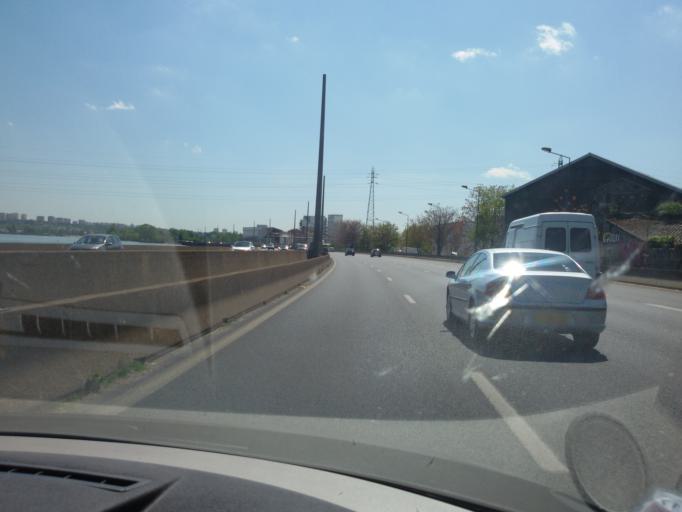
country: FR
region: Rhone-Alpes
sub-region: Departement du Rhone
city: Pierre-Benite
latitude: 45.7137
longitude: 4.8219
